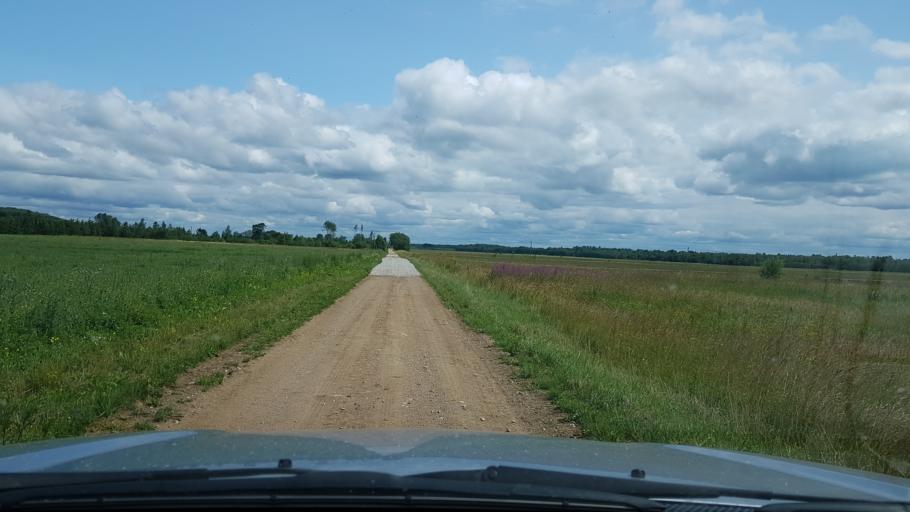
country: EE
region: Ida-Virumaa
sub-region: Sillamaee linn
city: Sillamae
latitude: 59.3681
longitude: 27.8493
